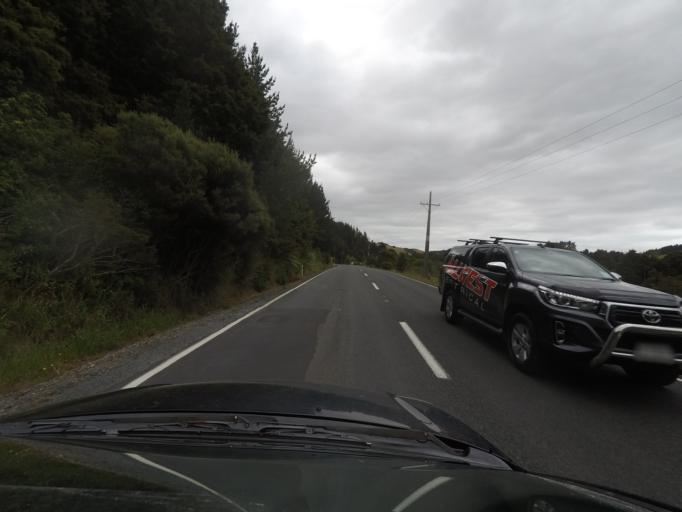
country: NZ
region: Auckland
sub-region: Auckland
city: Wellsford
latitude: -36.2895
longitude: 174.6137
